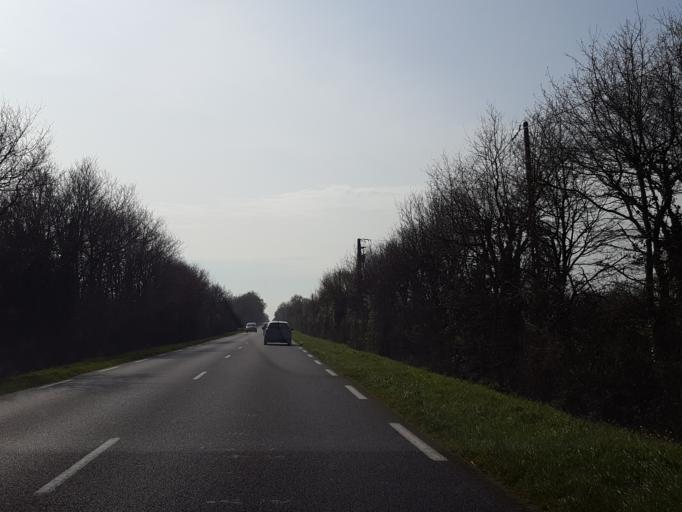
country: FR
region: Pays de la Loire
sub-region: Departement de la Vendee
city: Les Lucs-sur-Boulogne
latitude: 46.8253
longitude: -1.4752
